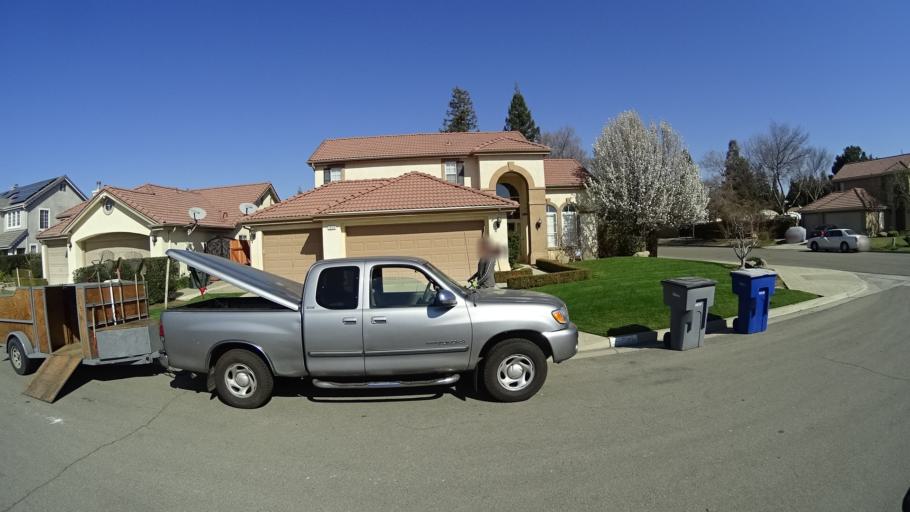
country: US
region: California
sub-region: Fresno County
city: Clovis
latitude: 36.8827
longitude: -119.7484
